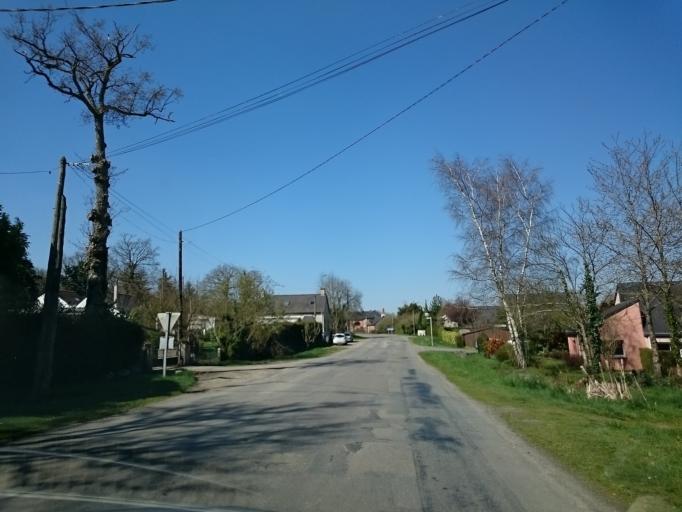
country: FR
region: Brittany
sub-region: Departement d'Ille-et-Vilaine
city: Laille
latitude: 47.9755
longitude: -1.6914
